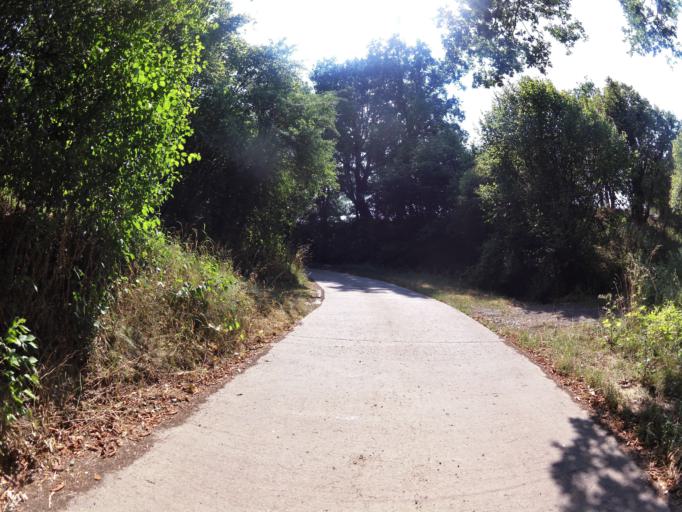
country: DE
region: Bavaria
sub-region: Regierungsbezirk Unterfranken
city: Ochsenfurt
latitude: 49.6521
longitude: 10.0590
